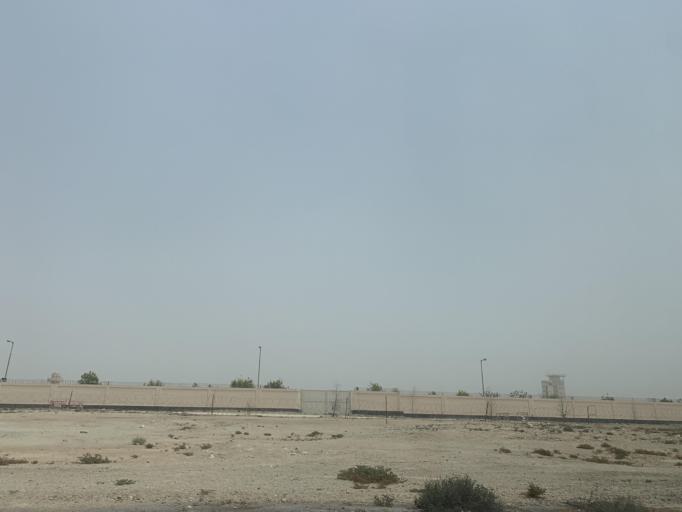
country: BH
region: Central Governorate
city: Madinat Hamad
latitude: 26.1617
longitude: 50.4822
